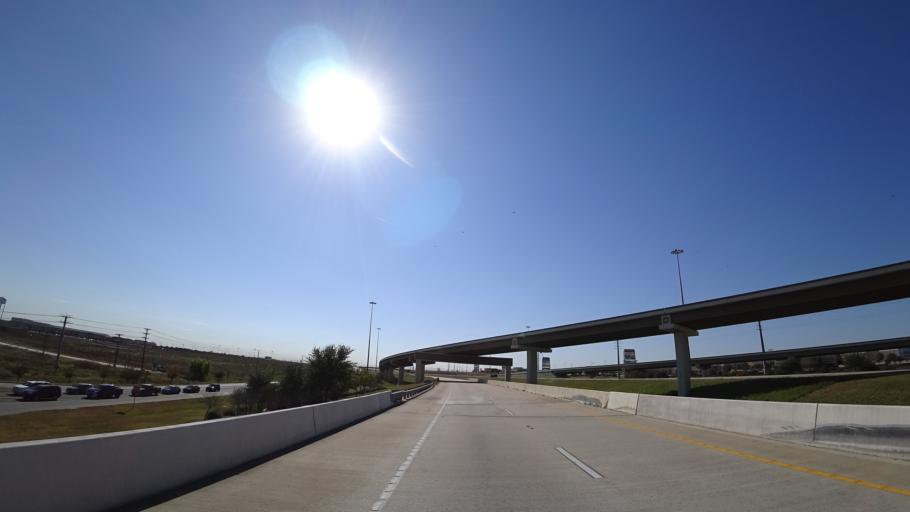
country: US
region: Texas
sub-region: Travis County
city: Pflugerville
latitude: 30.4721
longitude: -97.5923
